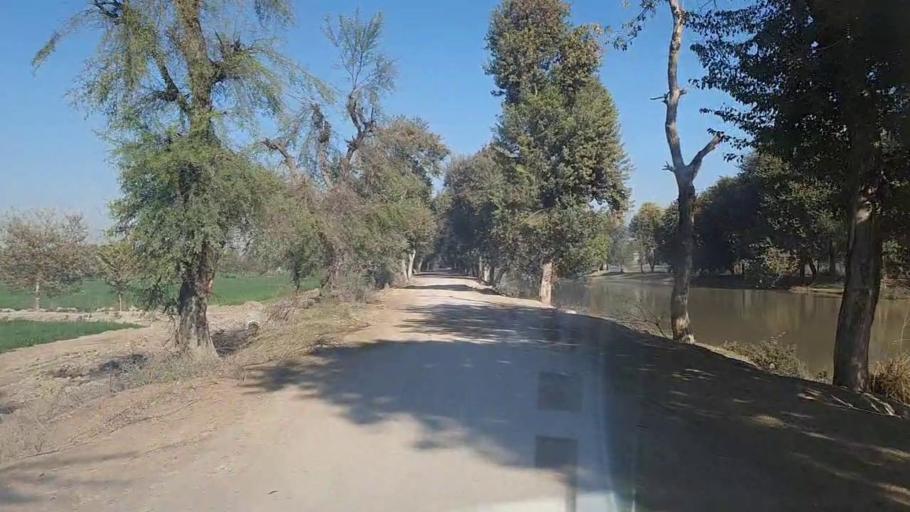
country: PK
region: Sindh
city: Khairpur
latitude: 27.9978
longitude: 69.6525
